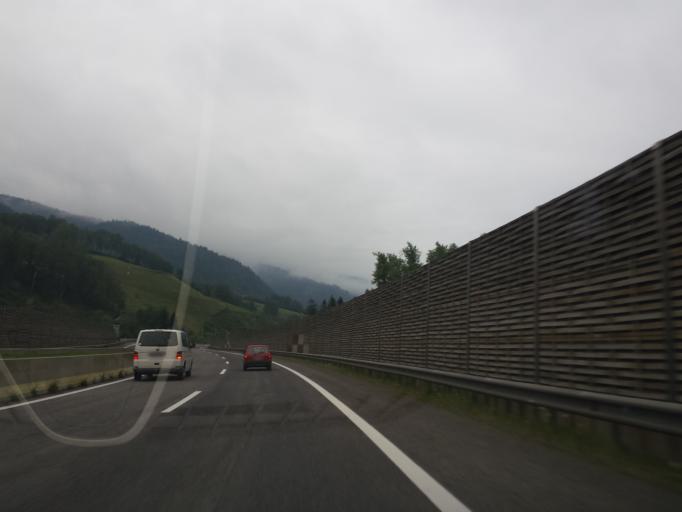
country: AT
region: Styria
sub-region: Politischer Bezirk Bruck-Muerzzuschlag
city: Spital am Semmering
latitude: 47.6029
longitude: 15.7310
